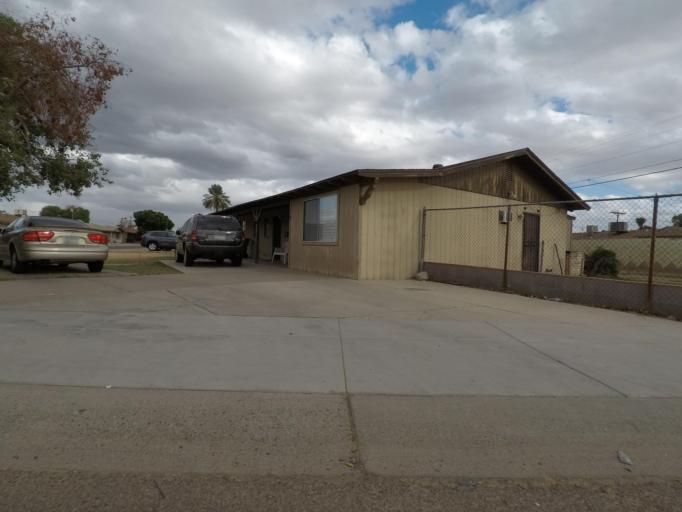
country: US
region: Arizona
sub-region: Maricopa County
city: Glendale
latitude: 33.4991
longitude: -112.1298
